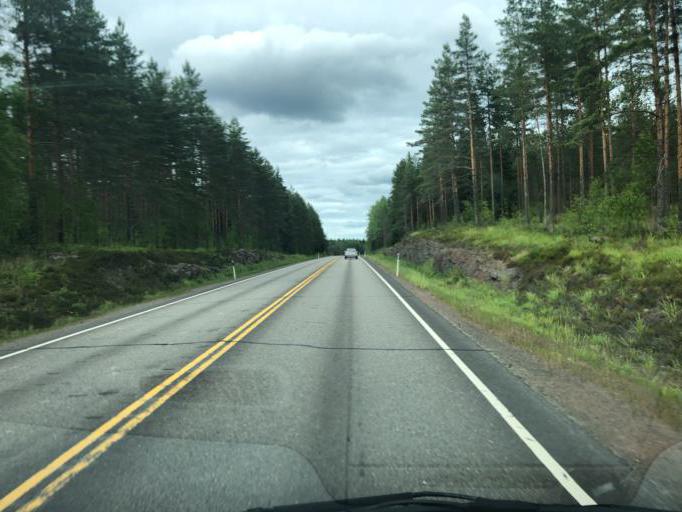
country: FI
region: Kymenlaakso
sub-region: Kouvola
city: Kouvola
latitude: 60.9896
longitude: 26.9190
